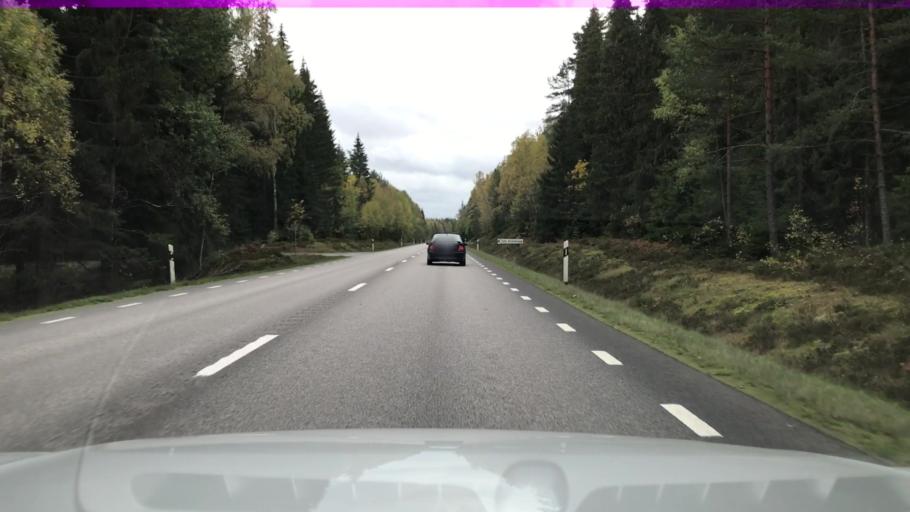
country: SE
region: Kalmar
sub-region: Hultsfreds Kommun
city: Hultsfred
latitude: 57.5478
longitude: 15.8456
